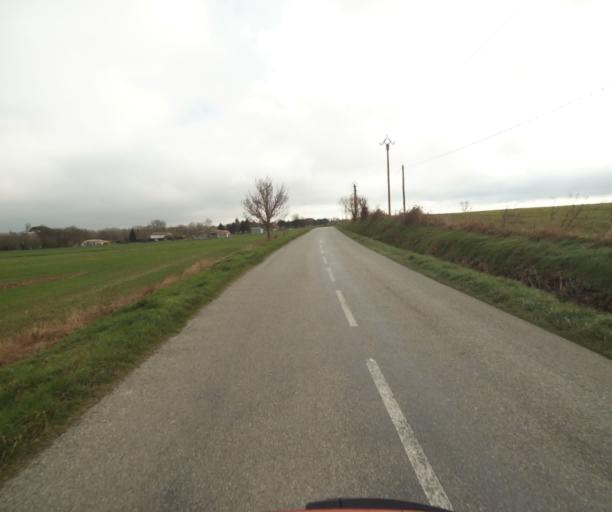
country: FR
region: Languedoc-Roussillon
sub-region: Departement de l'Aude
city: Belpech
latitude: 43.2050
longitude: 1.7316
